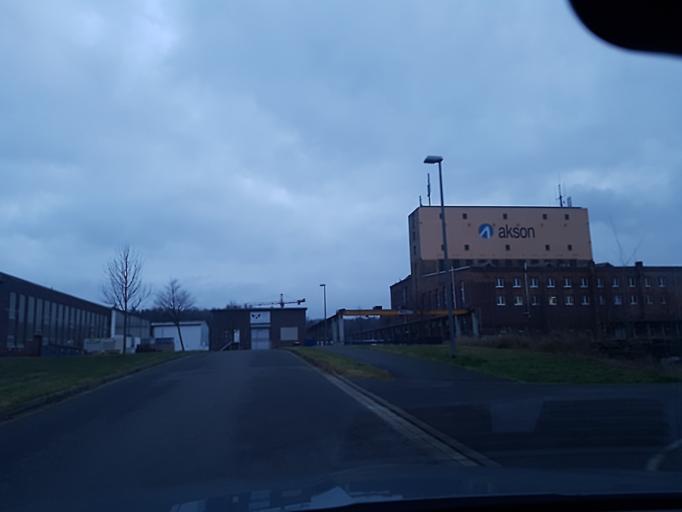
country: DE
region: Brandenburg
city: Trobitz
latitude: 51.5983
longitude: 13.4367
